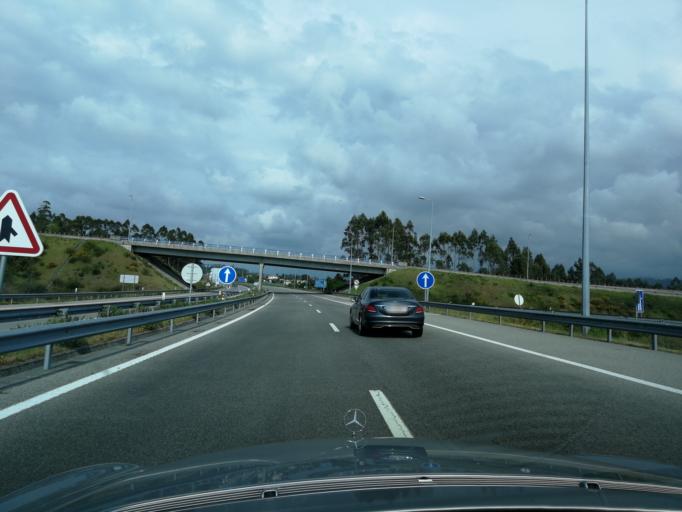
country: PT
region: Porto
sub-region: Vila do Conde
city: Arvore
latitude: 41.3873
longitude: -8.6984
